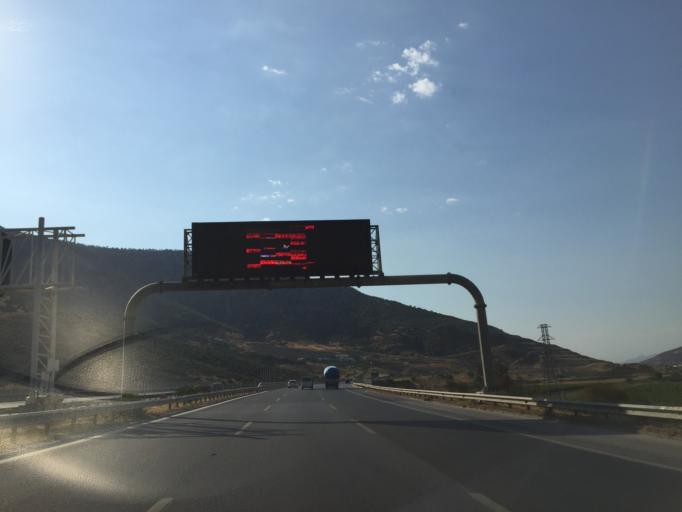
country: TR
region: Izmir
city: Belevi
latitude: 38.0291
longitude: 27.4347
